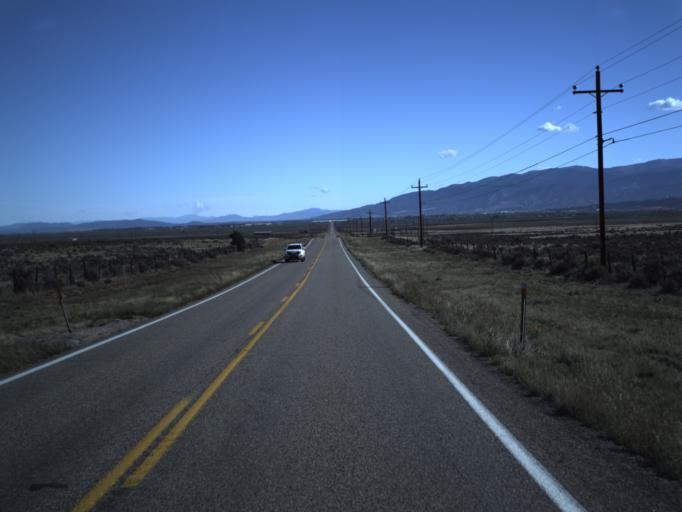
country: US
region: Utah
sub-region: Iron County
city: Cedar City
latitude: 37.6510
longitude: -113.2323
